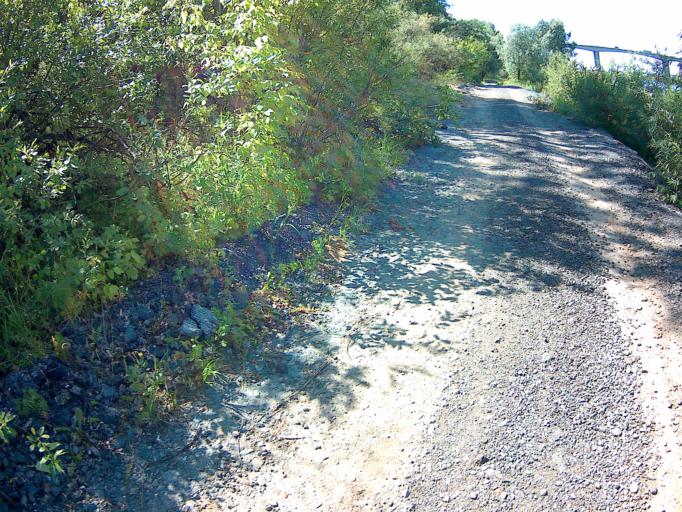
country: RU
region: Nizjnij Novgorod
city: Nizhniy Novgorod
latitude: 56.2525
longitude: 43.9574
